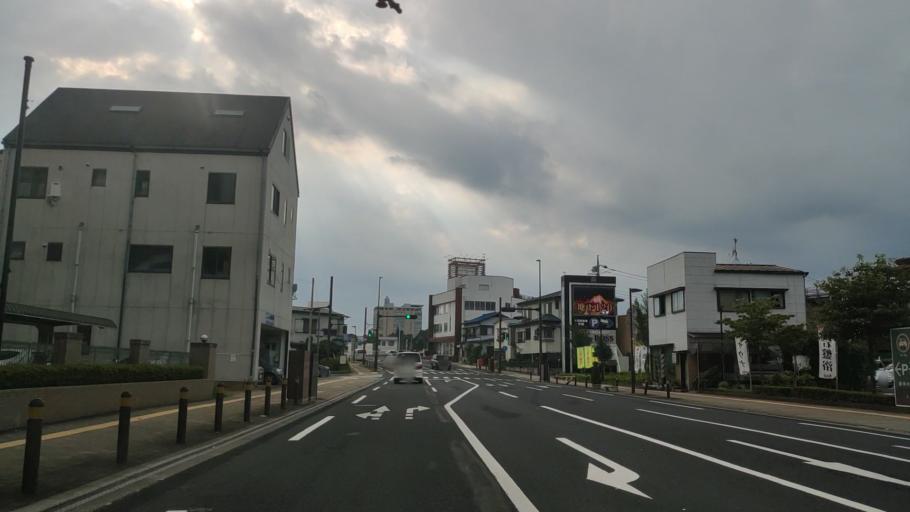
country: JP
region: Tochigi
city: Utsunomiya-shi
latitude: 36.5640
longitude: 139.8946
